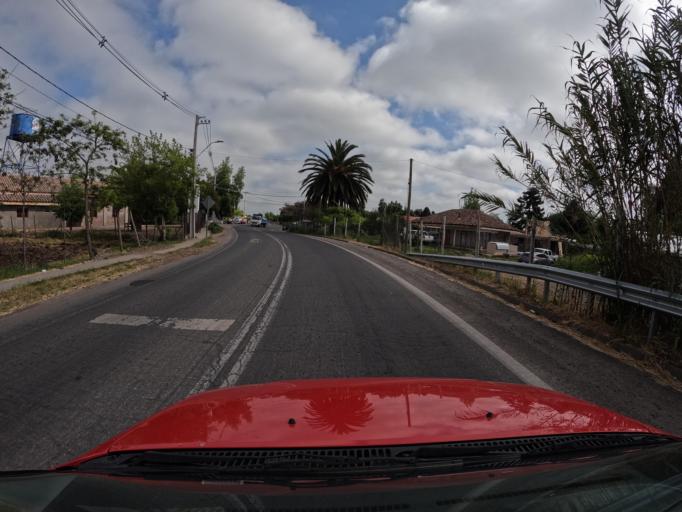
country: CL
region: O'Higgins
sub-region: Provincia de Colchagua
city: Santa Cruz
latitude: -34.6940
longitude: -71.3167
